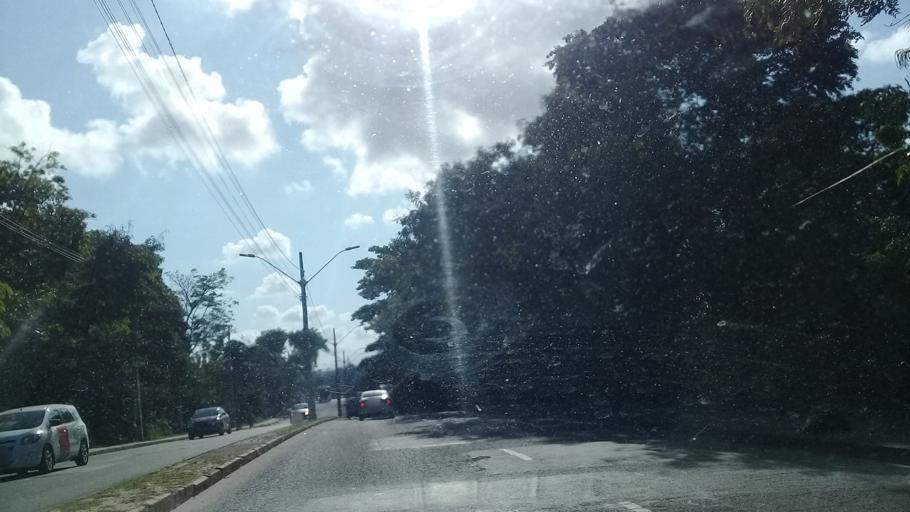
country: BR
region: Pernambuco
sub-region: Recife
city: Recife
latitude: -8.1081
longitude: -34.9324
